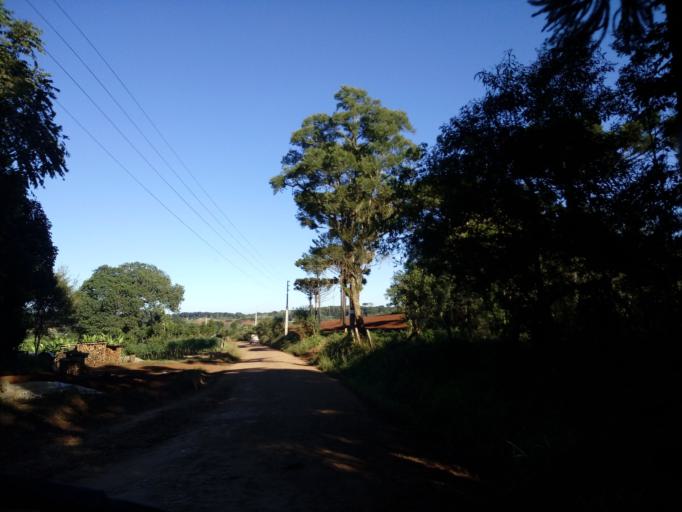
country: BR
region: Santa Catarina
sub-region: Chapeco
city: Chapeco
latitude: -27.1954
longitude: -52.6714
